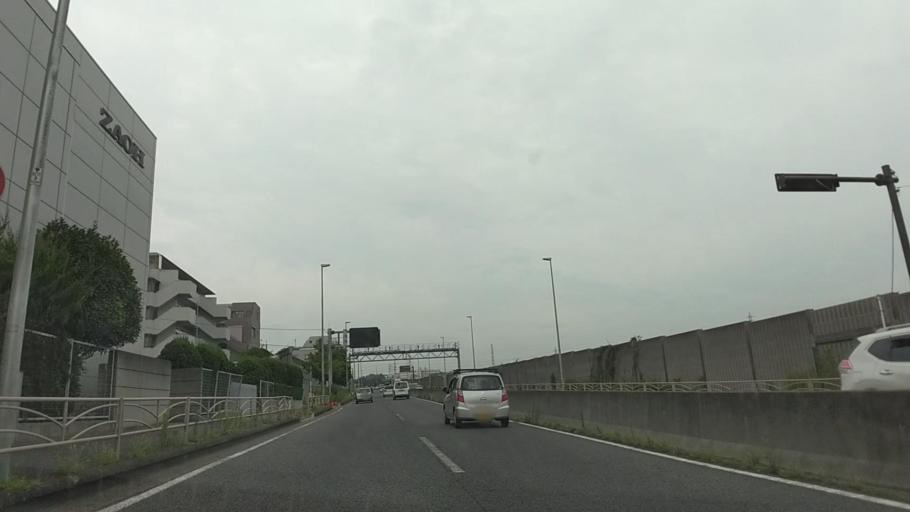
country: JP
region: Kanagawa
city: Fujisawa
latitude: 35.4092
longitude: 139.5305
